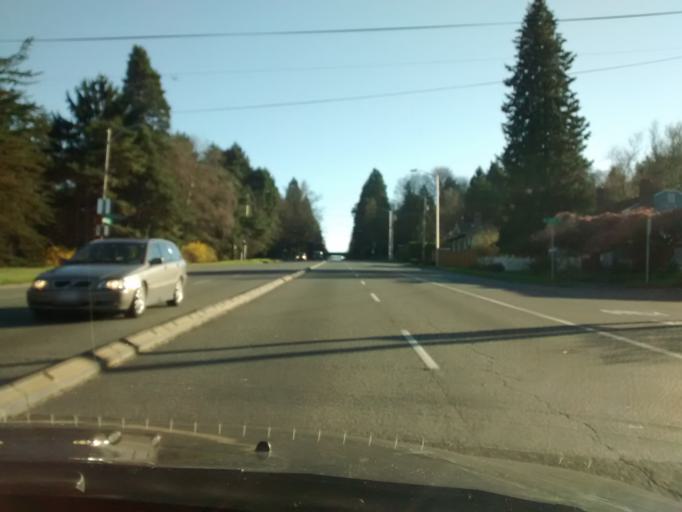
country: US
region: Washington
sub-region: King County
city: Seattle
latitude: 47.6733
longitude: -122.3473
